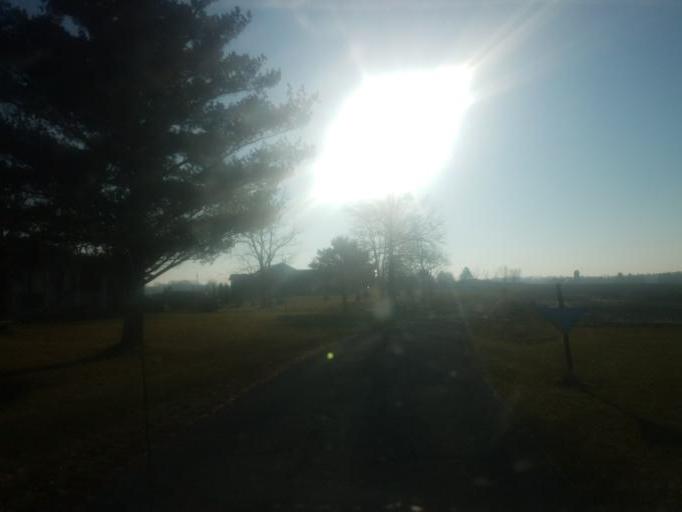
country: US
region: Ohio
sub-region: Crawford County
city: Bucyrus
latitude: 40.8354
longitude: -82.9477
